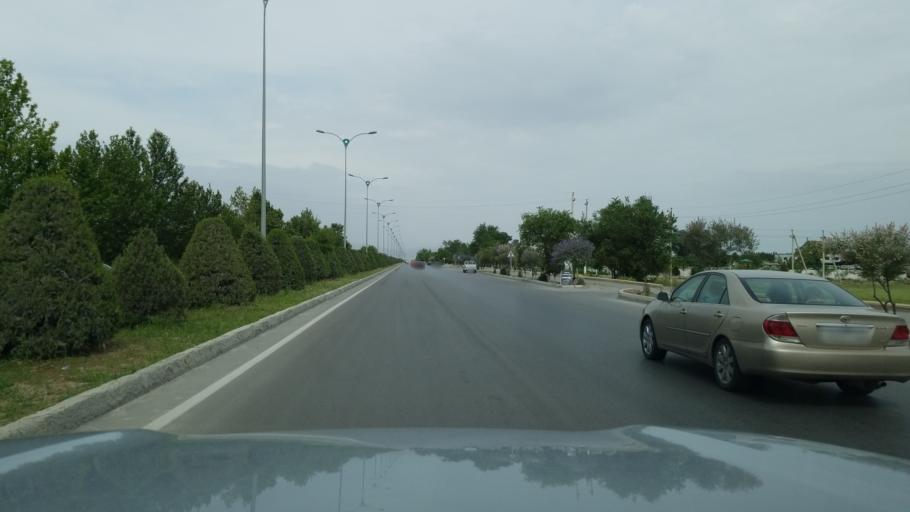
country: TM
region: Ahal
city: Abadan
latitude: 38.1631
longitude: 57.9453
